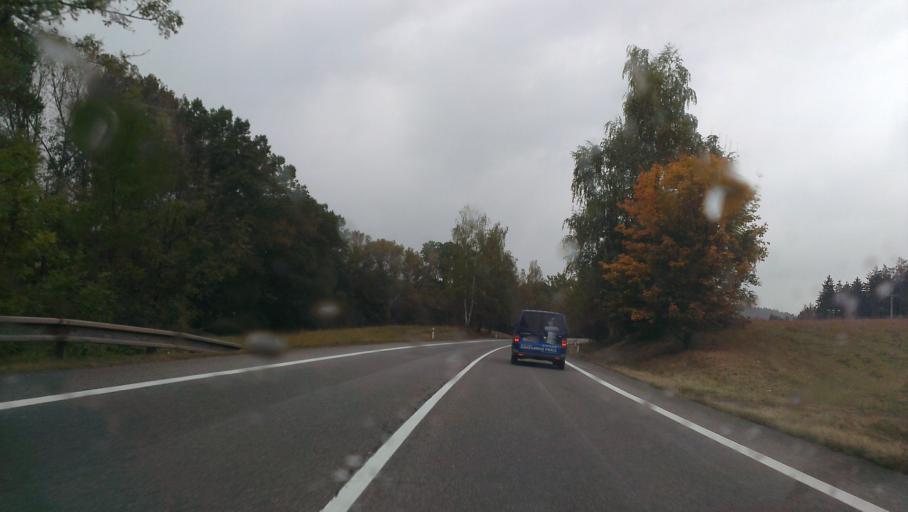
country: CZ
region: South Moravian
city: Cerna Hora
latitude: 49.4029
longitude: 16.5818
